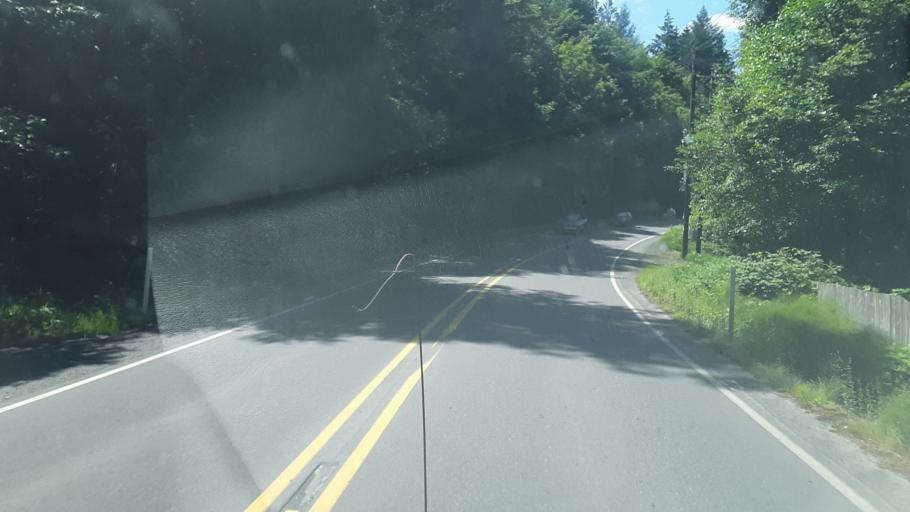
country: US
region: Washington
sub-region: Clark County
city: Amboy
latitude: 45.9100
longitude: -122.4480
